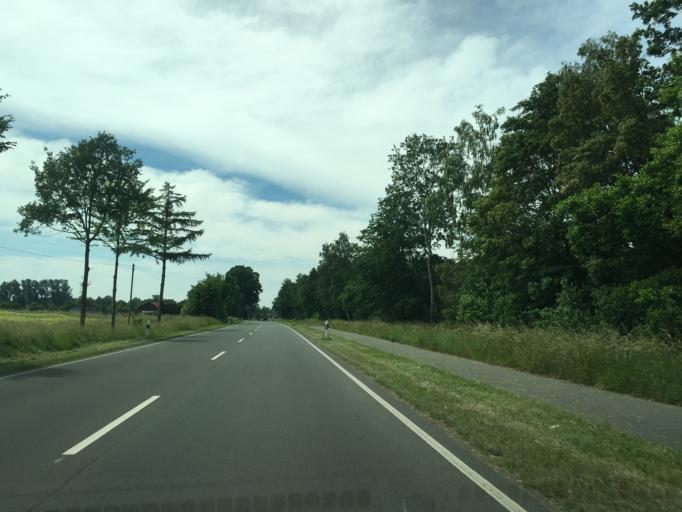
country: DE
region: North Rhine-Westphalia
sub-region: Regierungsbezirk Munster
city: Greven
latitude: 52.0894
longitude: 7.5420
